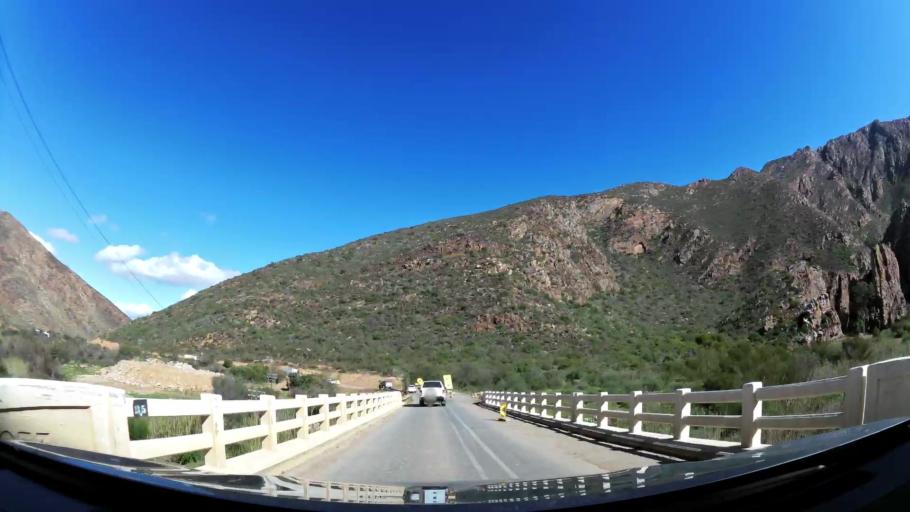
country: ZA
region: Western Cape
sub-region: Cape Winelands District Municipality
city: Ashton
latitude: -33.8032
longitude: 20.0944
